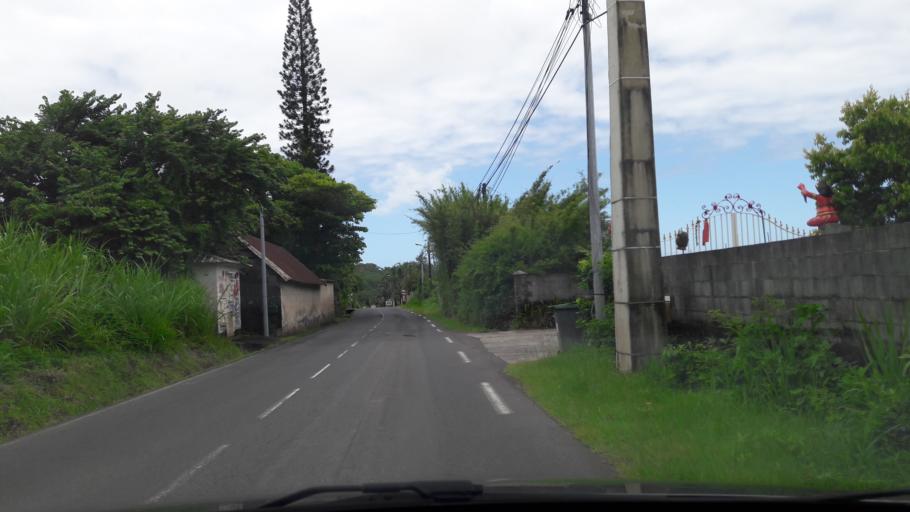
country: RE
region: Reunion
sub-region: Reunion
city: Saint-Andre
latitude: -20.9831
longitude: 55.6284
